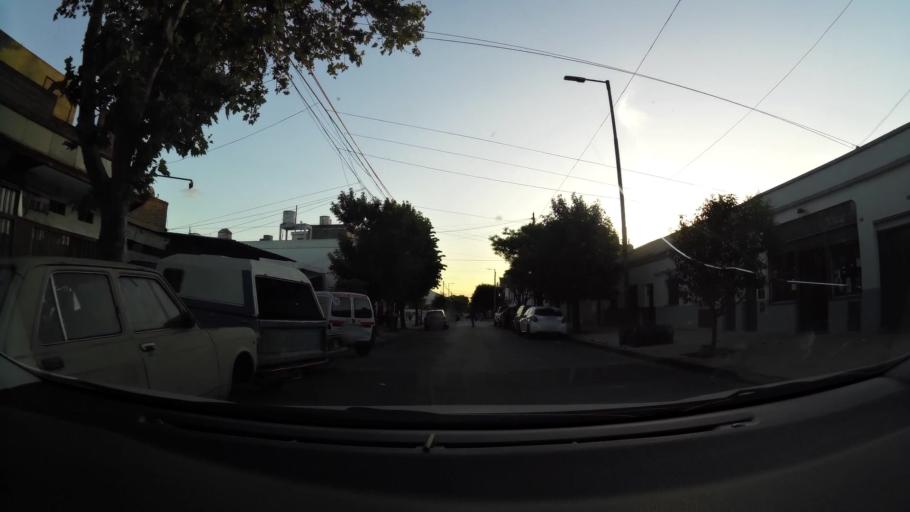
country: AR
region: Buenos Aires F.D.
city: Villa Lugano
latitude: -34.6694
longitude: -58.4711
